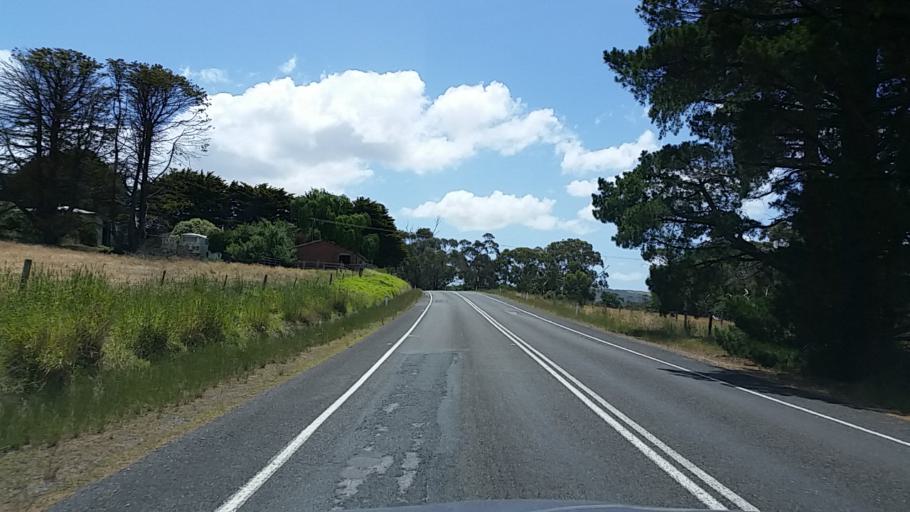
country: AU
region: South Australia
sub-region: Alexandrina
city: Mount Compass
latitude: -35.4378
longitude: 138.5944
